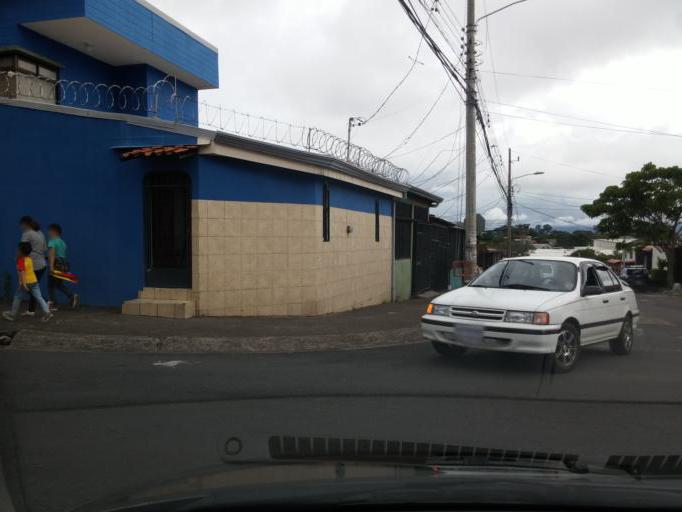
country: CR
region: Heredia
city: Mercedes
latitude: 10.0228
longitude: -84.1305
